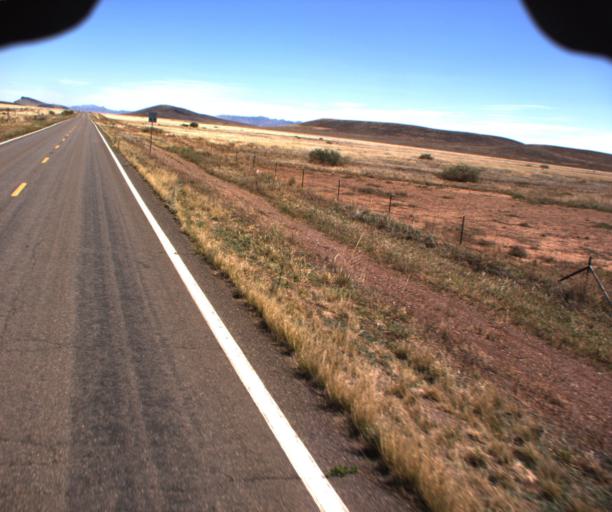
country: US
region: Arizona
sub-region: Cochise County
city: Douglas
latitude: 31.5950
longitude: -109.2382
